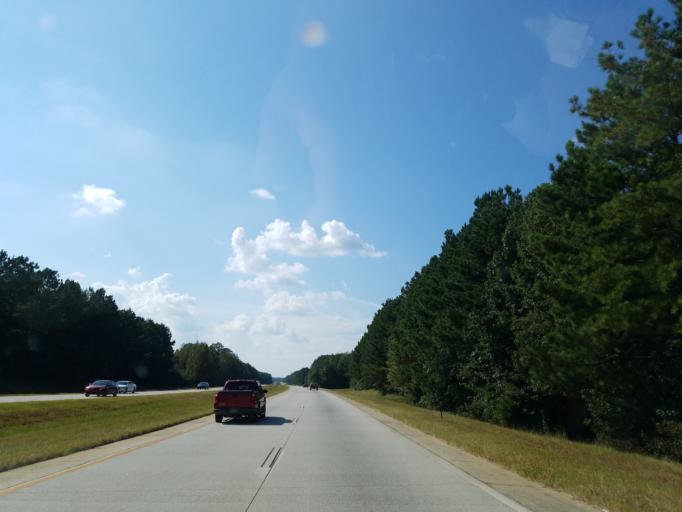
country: US
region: Georgia
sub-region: Oconee County
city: Bogart
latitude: 33.9325
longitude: -83.5315
